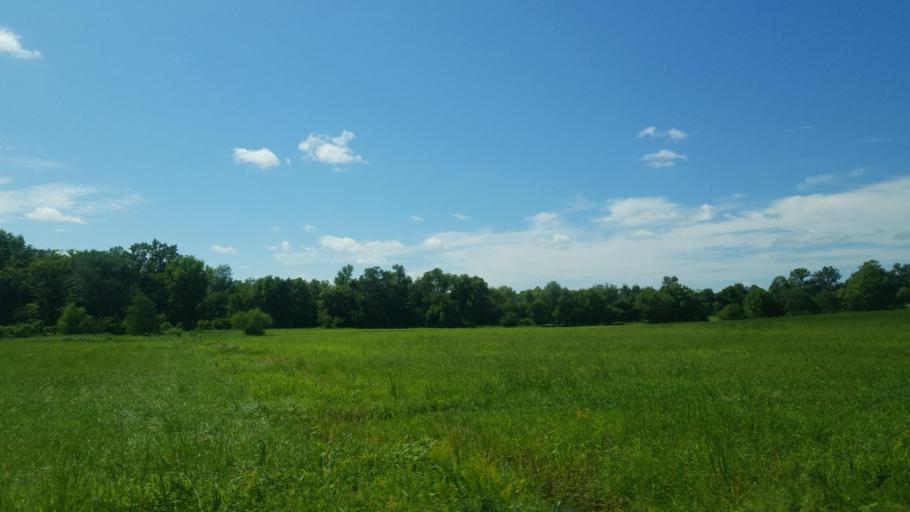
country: US
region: Illinois
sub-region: Williamson County
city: Johnston City
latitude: 37.7765
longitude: -88.8129
